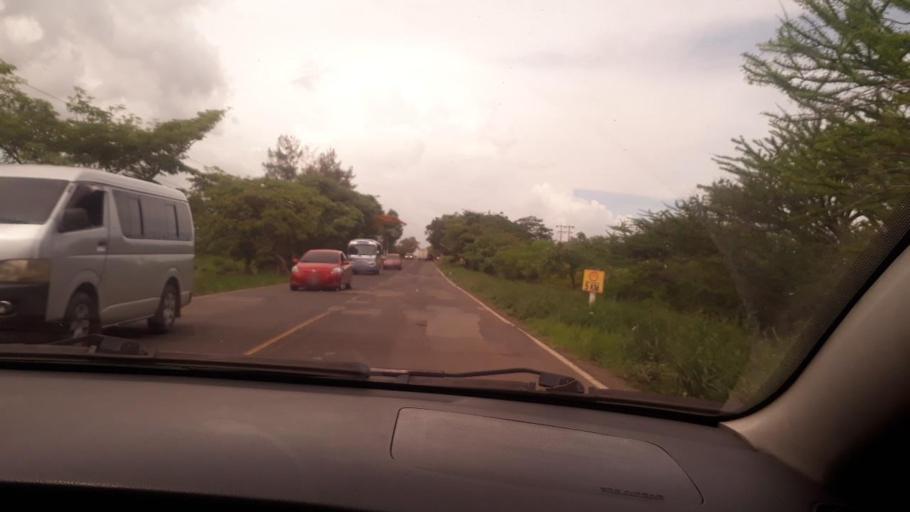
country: GT
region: Jutiapa
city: Jutiapa
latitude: 14.2885
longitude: -89.9369
